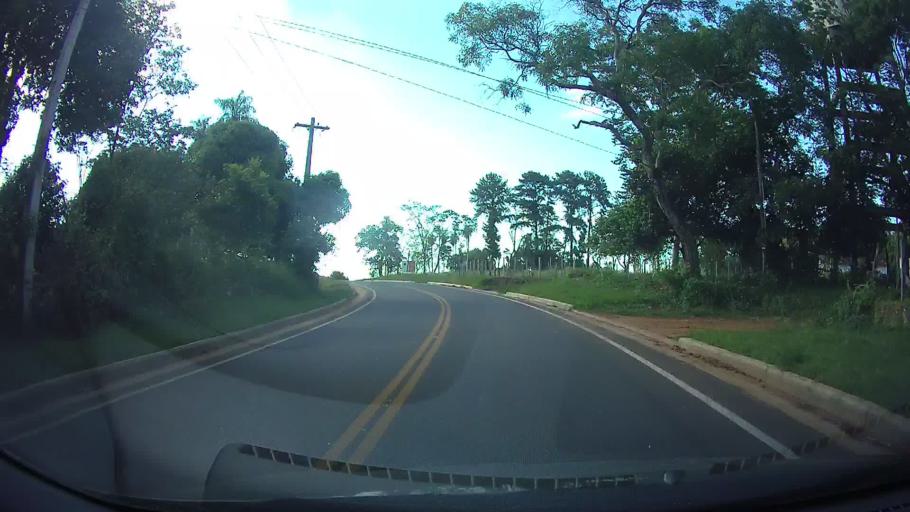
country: PY
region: Cordillera
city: Caacupe
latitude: -25.3679
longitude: -57.1430
